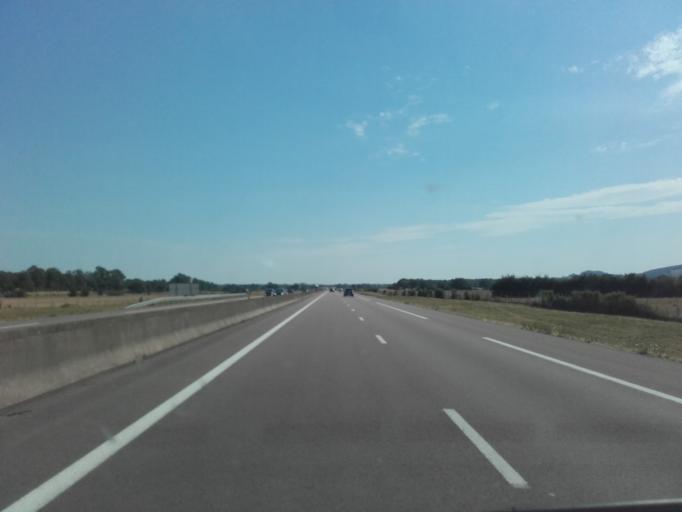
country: FR
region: Bourgogne
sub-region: Departement de la Cote-d'Or
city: Pouilly-en-Auxois
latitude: 47.2893
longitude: 4.5070
